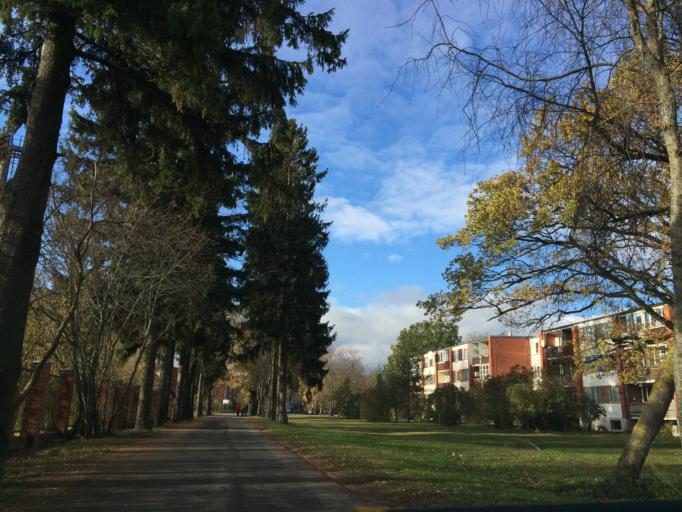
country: LV
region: Carnikava
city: Carnikava
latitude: 57.1302
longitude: 24.2700
